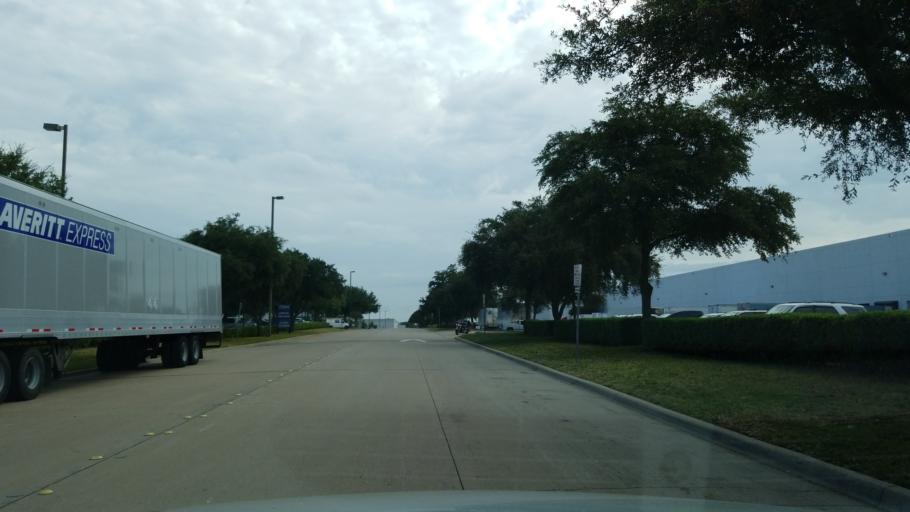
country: US
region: Texas
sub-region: Dallas County
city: Garland
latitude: 32.8916
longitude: -96.6929
